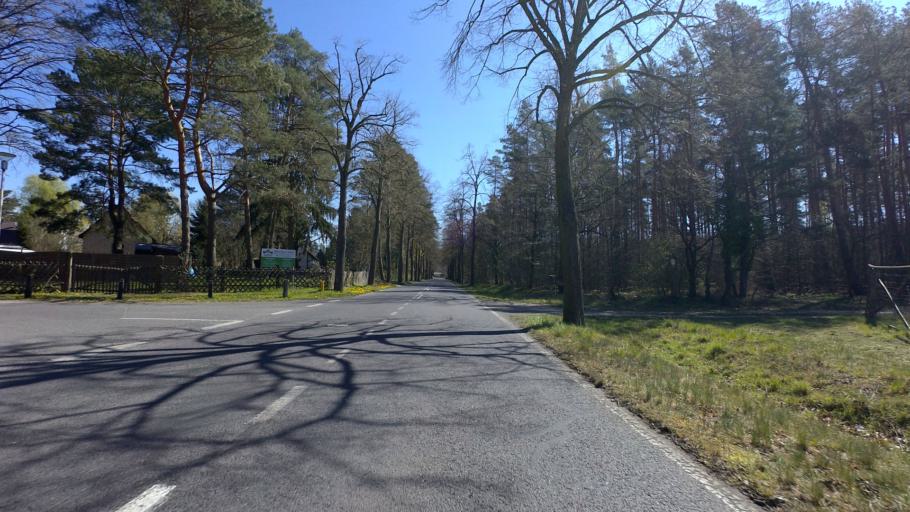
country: DE
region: Brandenburg
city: Schulzendorf
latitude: 52.3387
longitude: 13.5939
